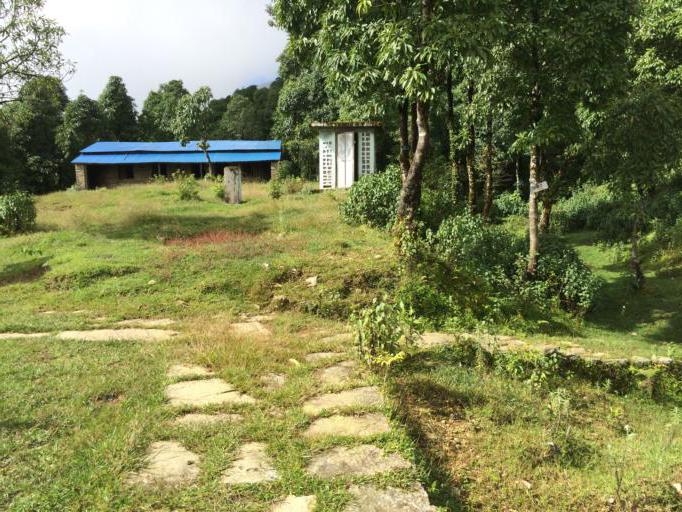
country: NP
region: Western Region
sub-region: Gandaki Zone
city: Pokhara
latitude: 28.2415
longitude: 83.8118
